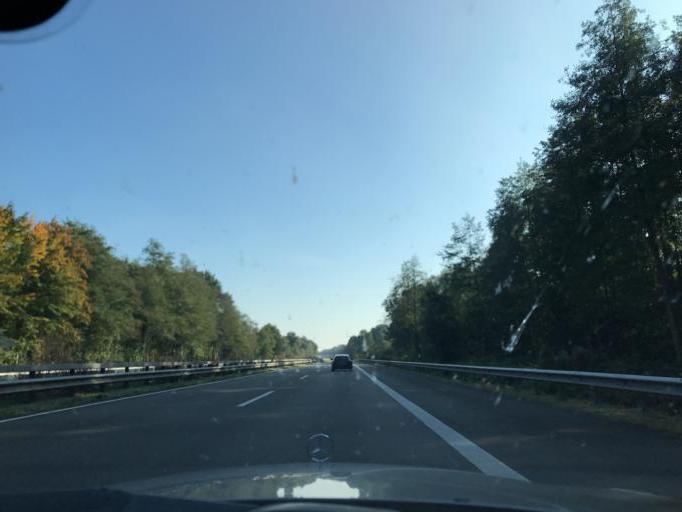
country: DE
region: Lower Saxony
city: Bad Zwischenahn
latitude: 53.2348
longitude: 8.0289
